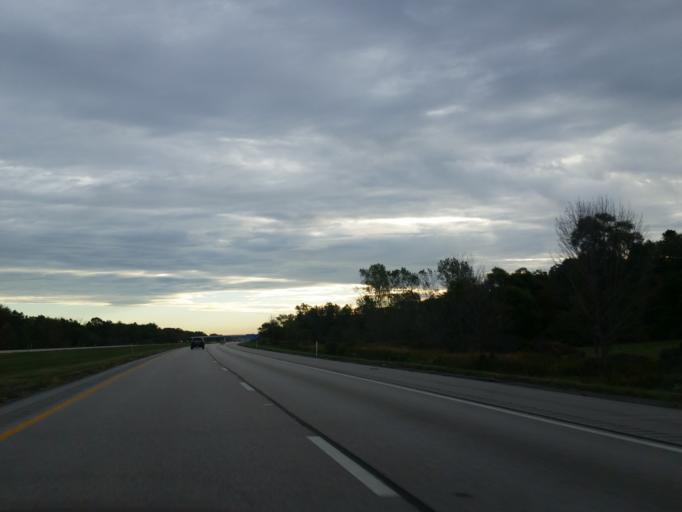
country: US
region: Ohio
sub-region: Ashtabula County
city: Conneaut
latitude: 41.9083
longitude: -80.6002
